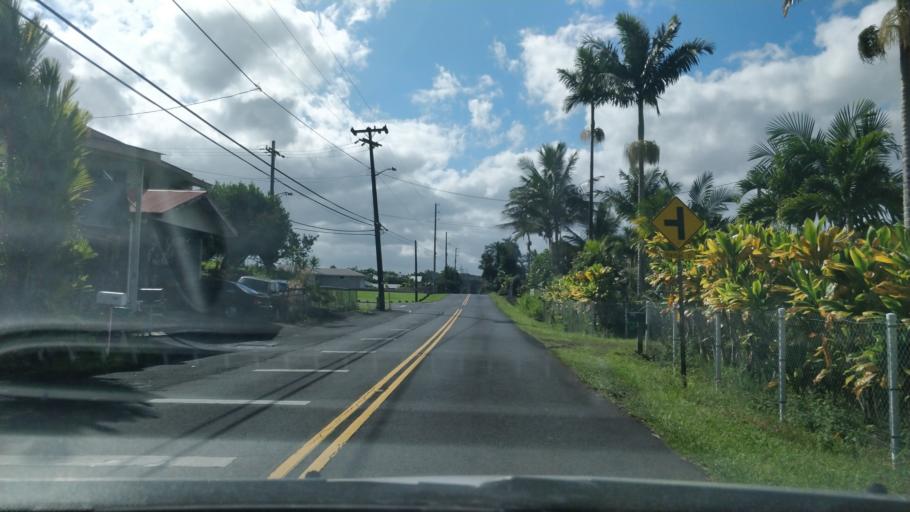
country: US
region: Hawaii
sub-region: Hawaii County
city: Hilo
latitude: 19.6724
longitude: -155.1058
